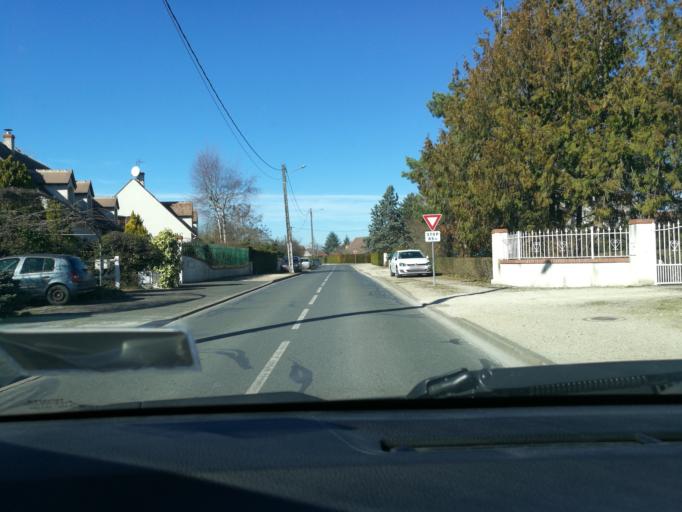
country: FR
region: Centre
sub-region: Departement du Loiret
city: Saint-Jean-le-Blanc
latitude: 47.8746
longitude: 1.9257
